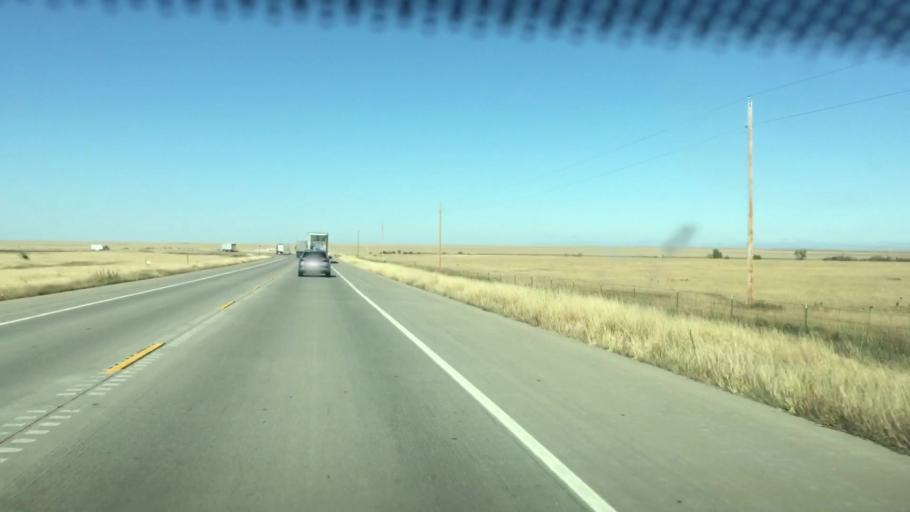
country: US
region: Colorado
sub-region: Kiowa County
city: Eads
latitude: 38.3440
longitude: -102.7169
